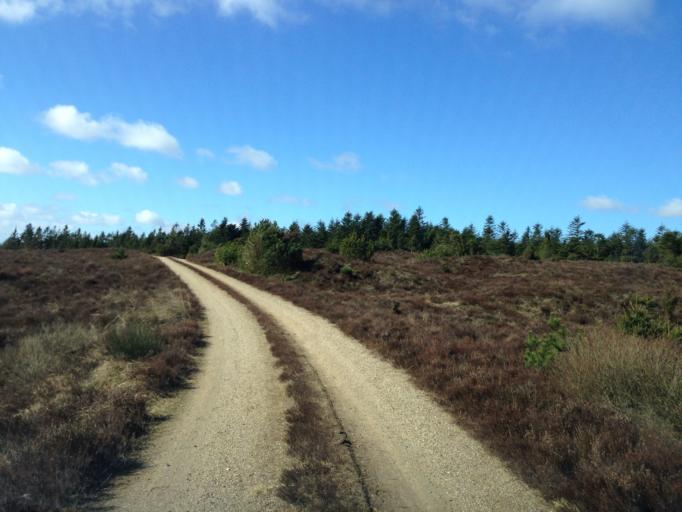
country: DK
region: Central Jutland
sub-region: Holstebro Kommune
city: Ulfborg
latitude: 56.2511
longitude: 8.4323
